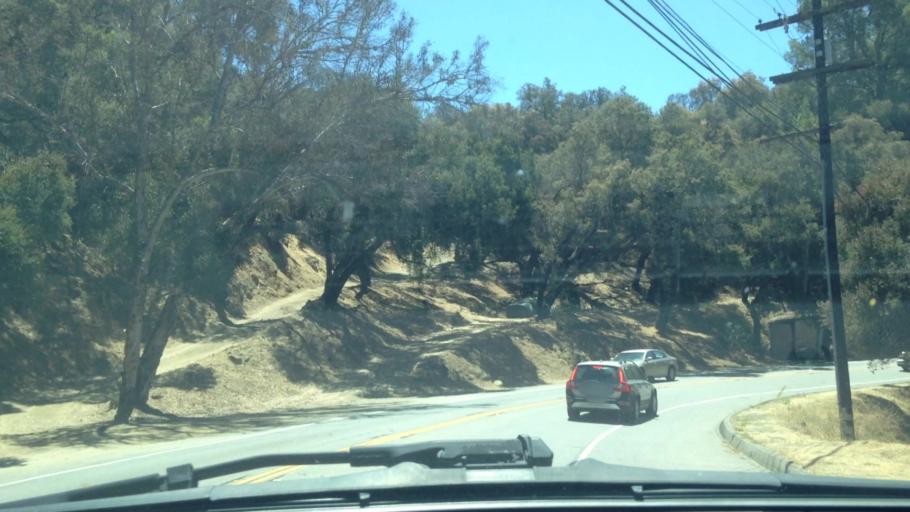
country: US
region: California
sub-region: Los Angeles County
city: Topanga
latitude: 34.1028
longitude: -118.5917
